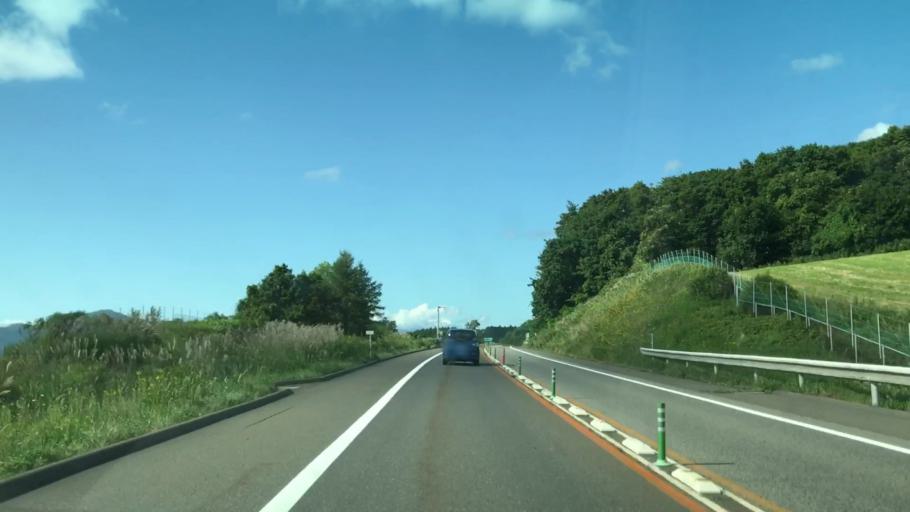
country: JP
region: Hokkaido
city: Date
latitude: 42.4482
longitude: 140.9137
